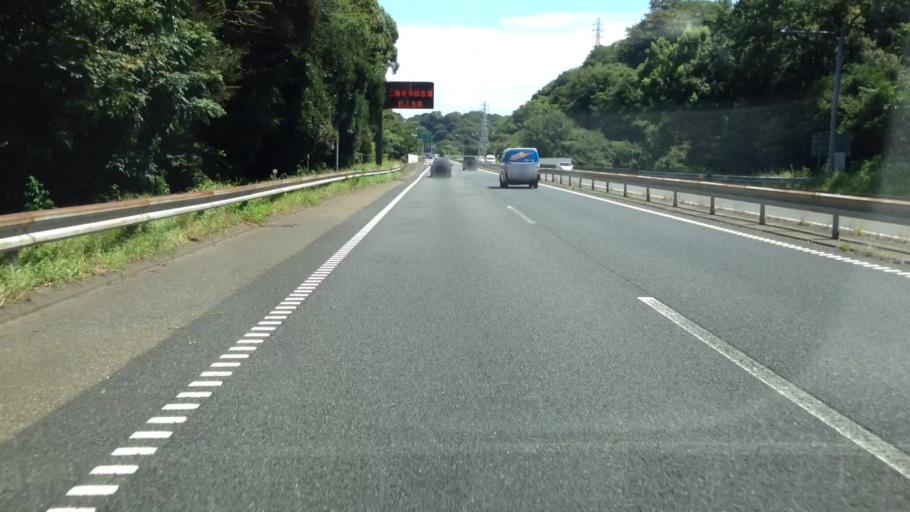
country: JP
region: Kanagawa
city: Yokosuka
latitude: 35.2438
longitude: 139.6539
